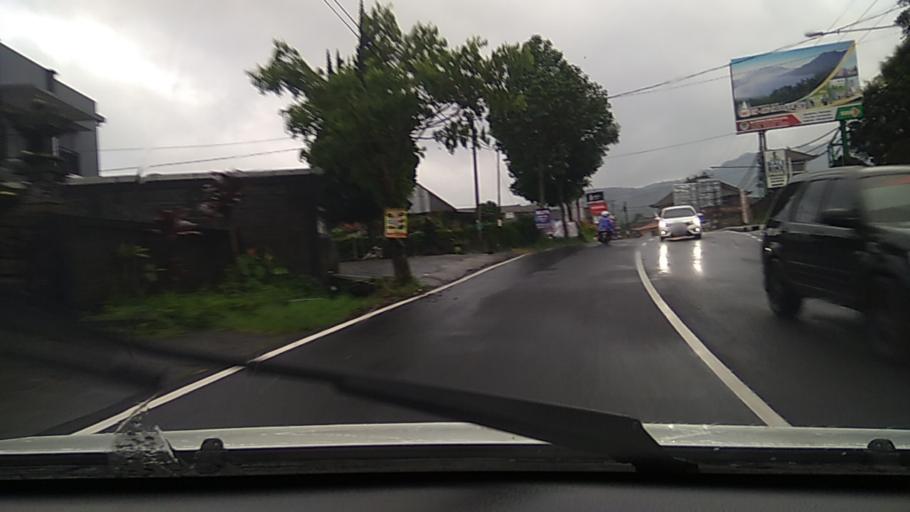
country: ID
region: Bali
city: Munduk
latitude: -8.2469
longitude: 115.1515
